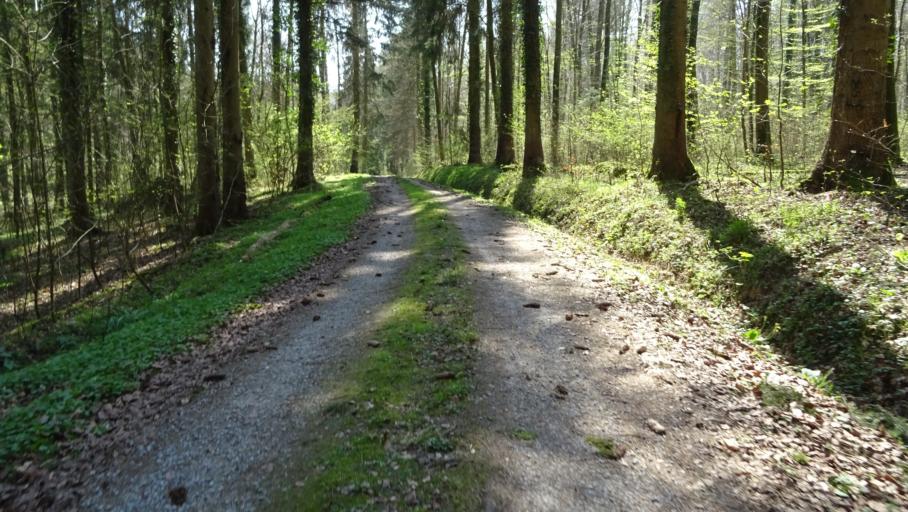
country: DE
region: Baden-Wuerttemberg
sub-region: Karlsruhe Region
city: Obrigheim
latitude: 49.3726
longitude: 9.1021
